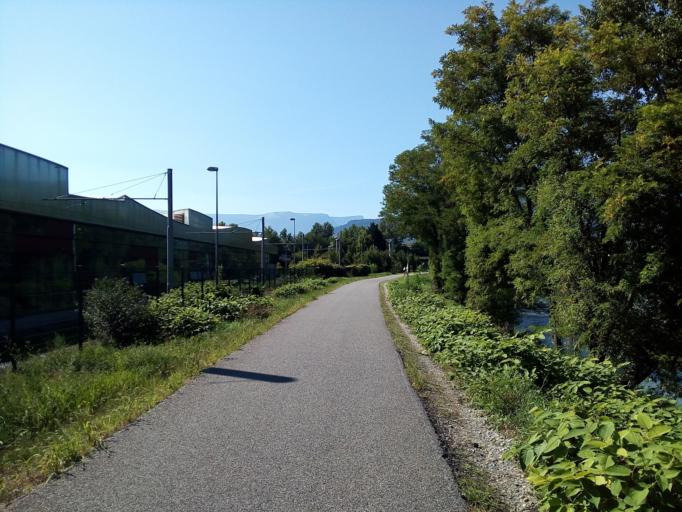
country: FR
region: Rhone-Alpes
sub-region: Departement de l'Isere
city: Gieres
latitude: 45.1899
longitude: 5.7845
